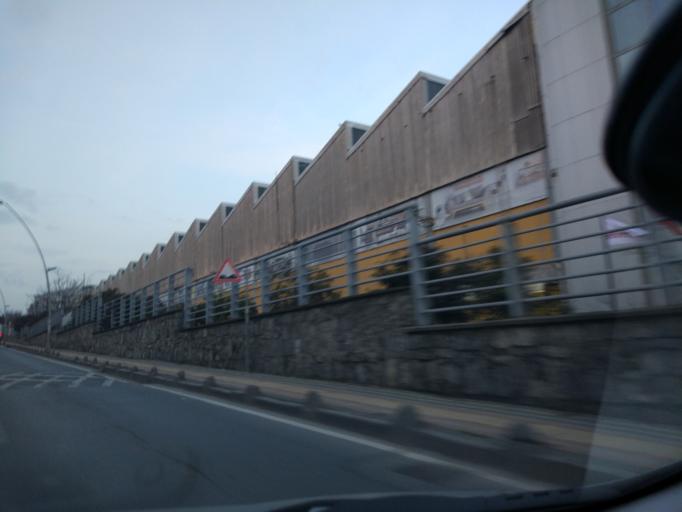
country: TR
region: Istanbul
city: Bahcelievler
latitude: 41.0052
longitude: 28.8216
